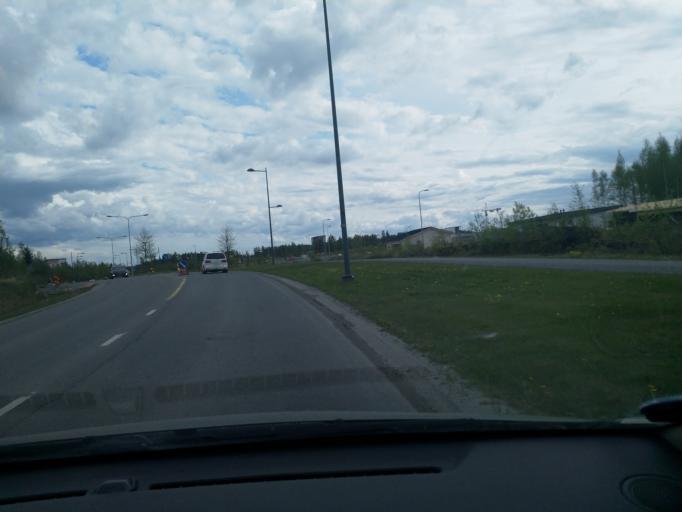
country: FI
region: Pirkanmaa
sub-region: Tampere
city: Tampere
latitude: 61.4447
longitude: 23.8060
